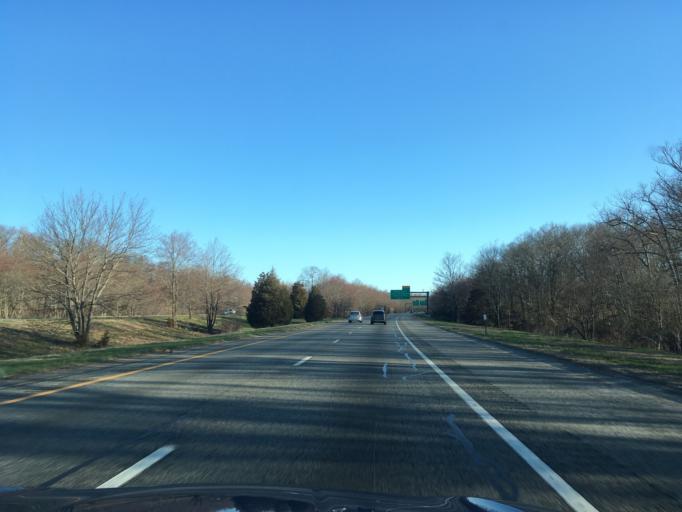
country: US
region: Rhode Island
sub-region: Providence County
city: Johnston
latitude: 41.7962
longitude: -71.5090
